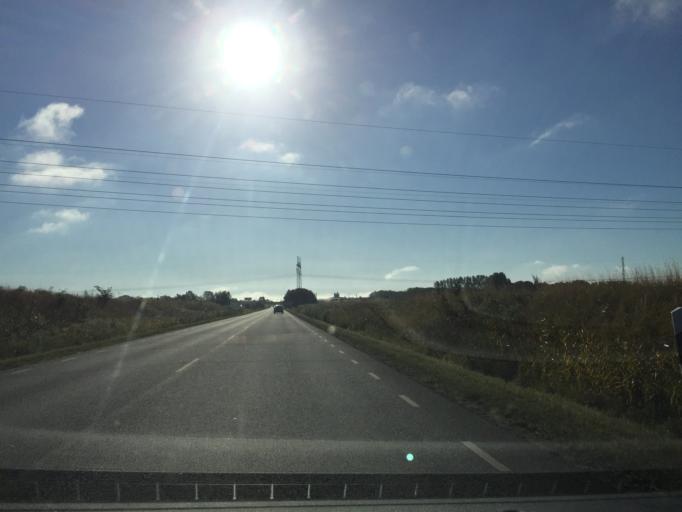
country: SE
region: Skane
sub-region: Staffanstorps Kommun
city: Staffanstorp
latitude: 55.6615
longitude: 13.2109
